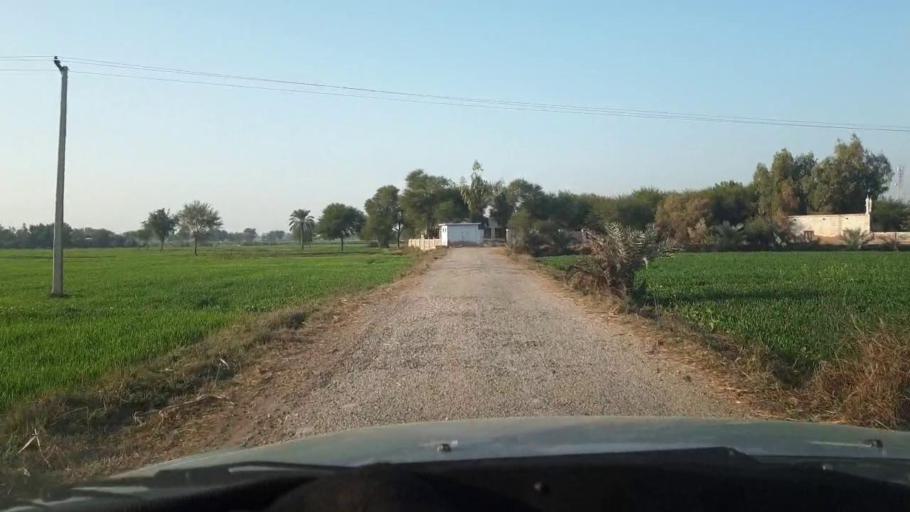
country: PK
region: Sindh
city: Mirpur Mathelo
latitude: 27.9829
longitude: 69.6279
